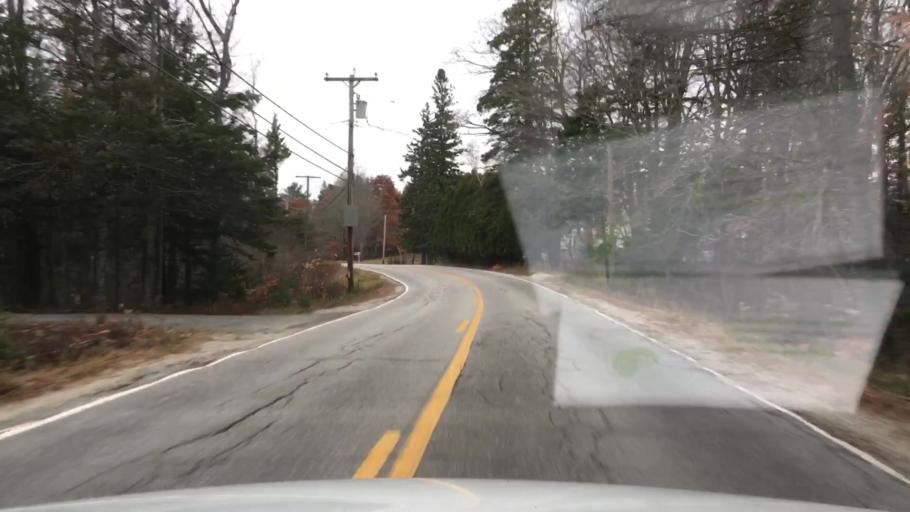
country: US
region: Maine
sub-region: Hancock County
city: Sedgwick
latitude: 44.3677
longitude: -68.5541
